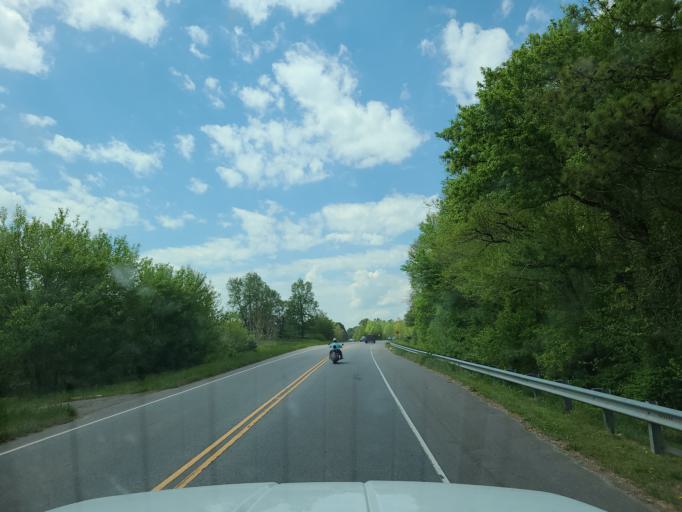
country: US
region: North Carolina
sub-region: Lincoln County
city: Lincolnton
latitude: 35.4289
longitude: -81.2930
